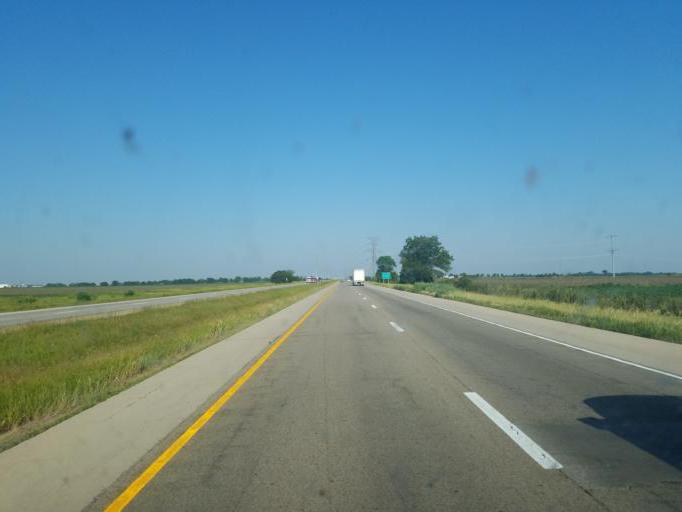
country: US
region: Illinois
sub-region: LaSalle County
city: Seneca
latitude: 41.3775
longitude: -88.5317
